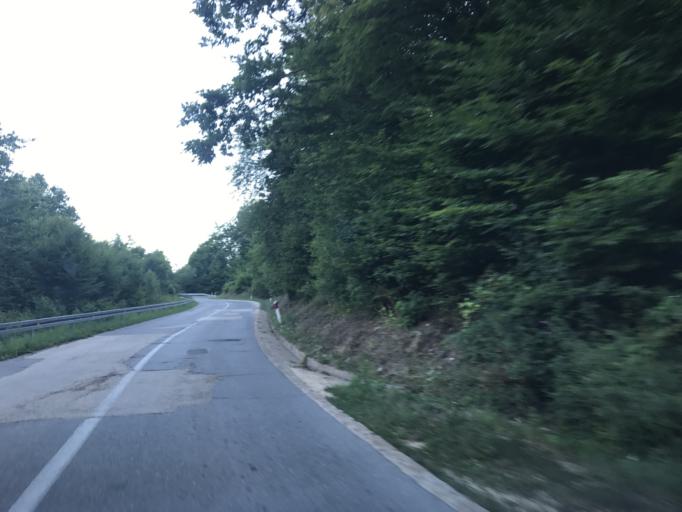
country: RO
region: Mehedinti
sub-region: Comuna Gogosu
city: Ostrovu Mare
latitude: 44.2918
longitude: 22.2777
